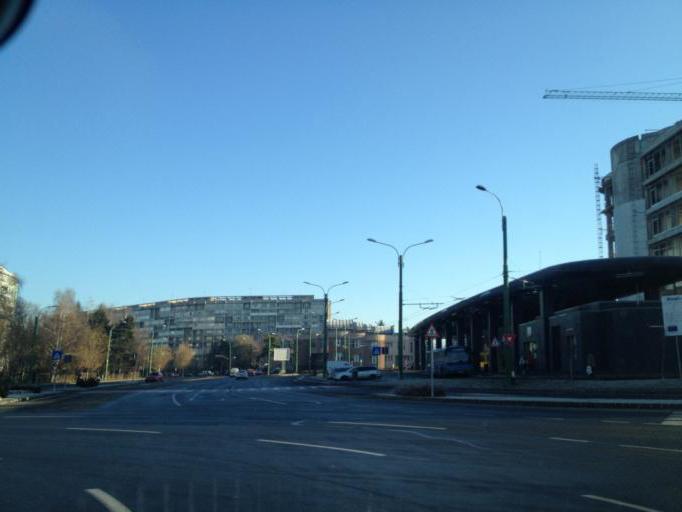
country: RO
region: Brasov
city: Brasov
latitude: 45.6342
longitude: 25.6344
